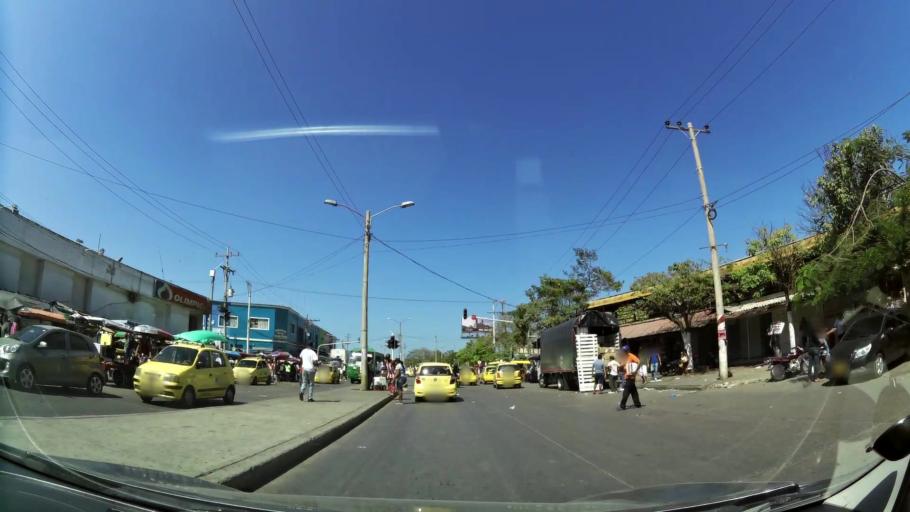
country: CO
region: Atlantico
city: Barranquilla
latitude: 10.9807
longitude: -74.7754
